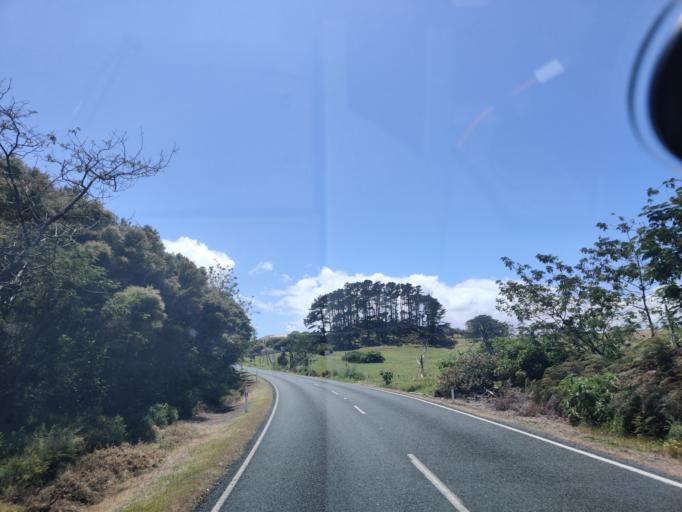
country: NZ
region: Northland
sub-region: Far North District
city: Kaitaia
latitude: -35.0326
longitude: 173.1845
